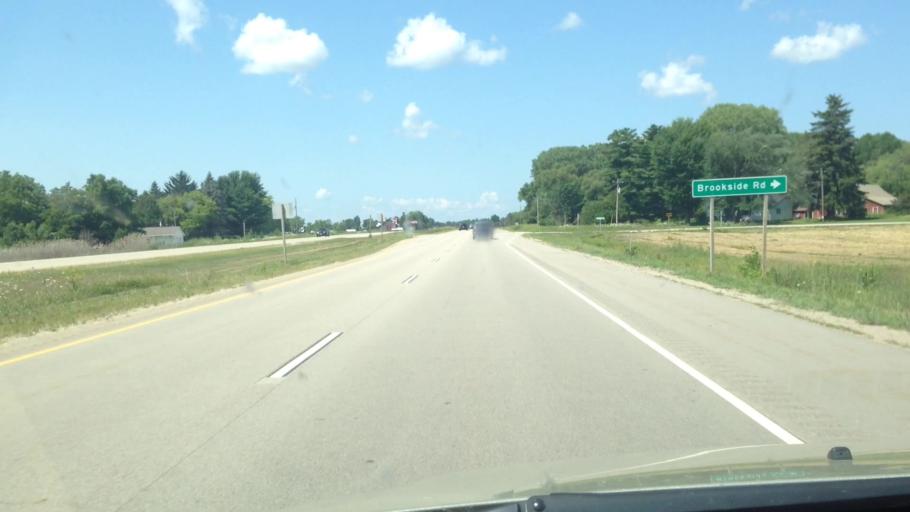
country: US
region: Wisconsin
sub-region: Oconto County
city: Oconto Falls
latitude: 44.8007
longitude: -88.0045
